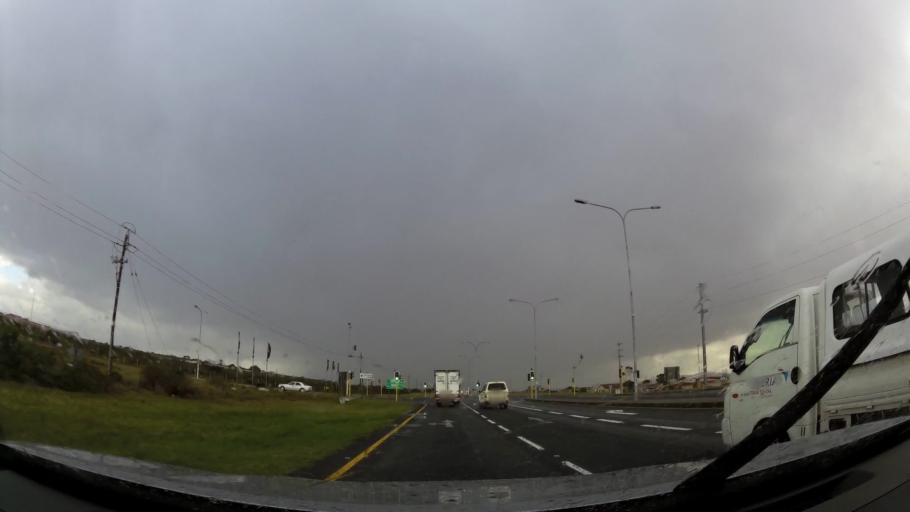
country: ZA
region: Western Cape
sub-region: Eden District Municipality
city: Mossel Bay
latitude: -34.1828
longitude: 22.0911
